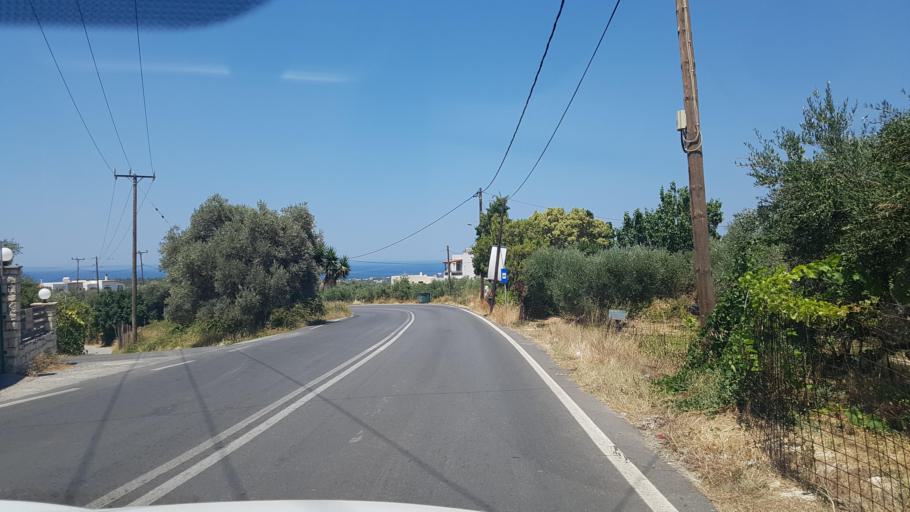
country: GR
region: Crete
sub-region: Nomos Rethymnis
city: Agia Foteini
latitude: 35.3525
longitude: 24.5892
